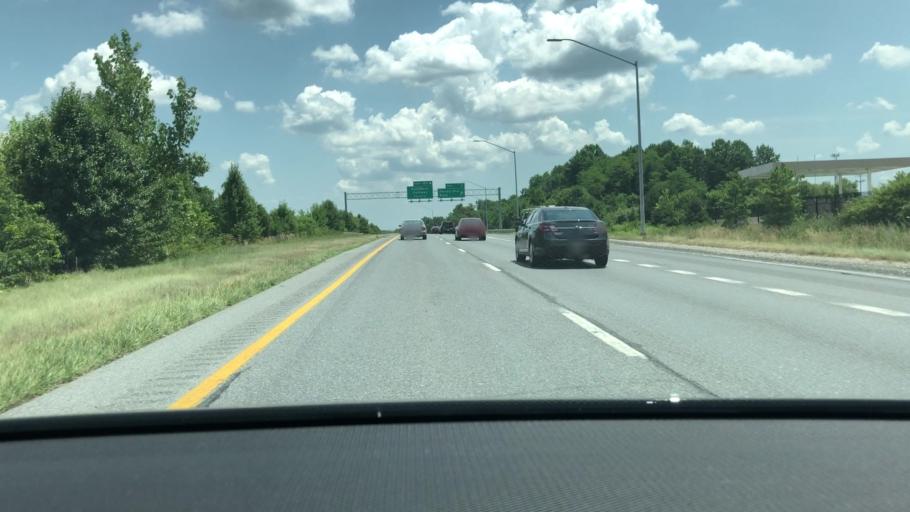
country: US
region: Maryland
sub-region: Howard County
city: Fort George G Mead Junction
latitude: 39.1319
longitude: -76.8016
